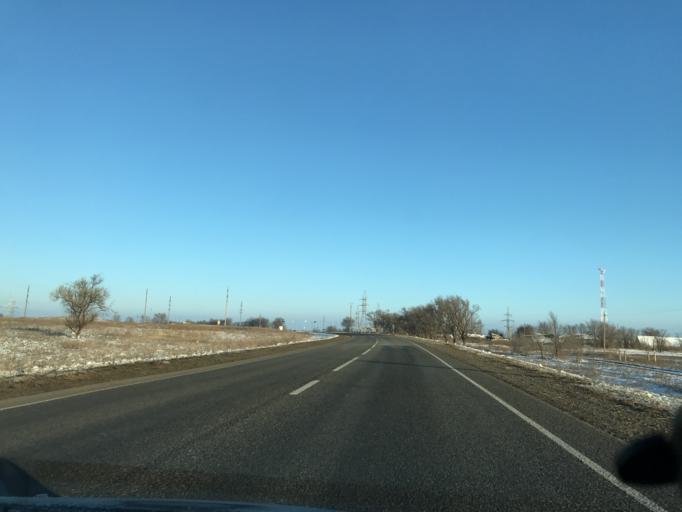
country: RU
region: Stavropol'skiy
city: Bezopasnoye
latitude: 45.6132
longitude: 41.9418
